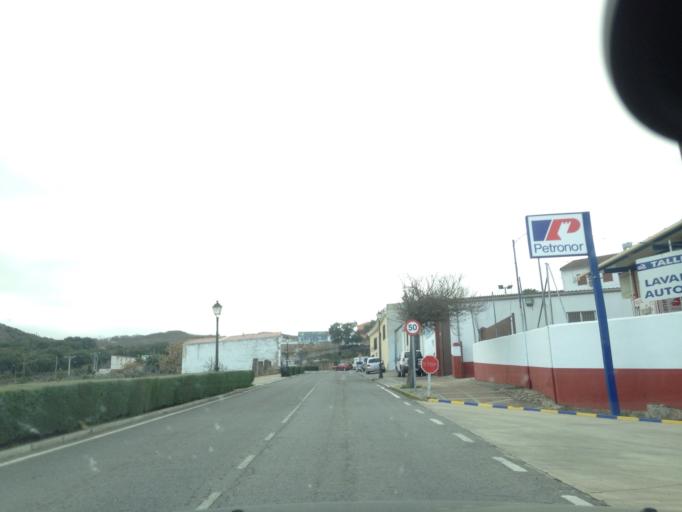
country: ES
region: Extremadura
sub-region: Provincia de Caceres
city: Montanchez
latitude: 39.2290
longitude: -6.1485
